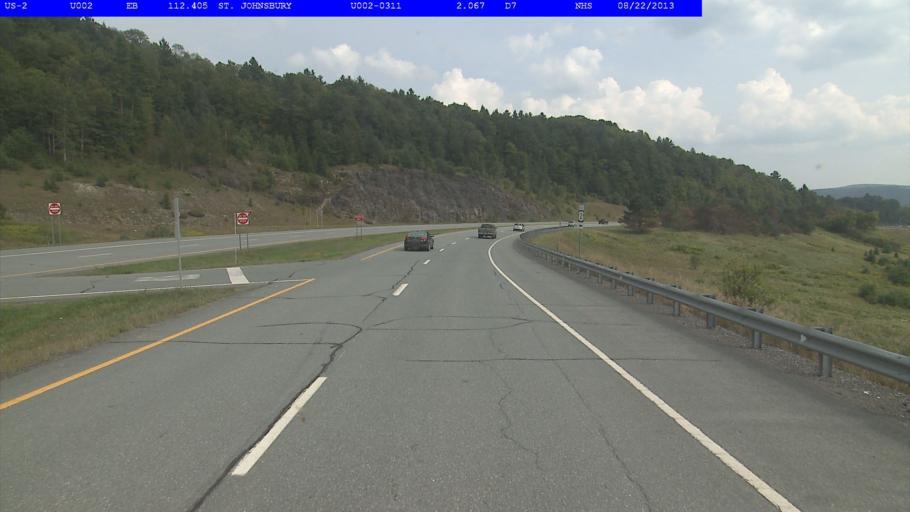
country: US
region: Vermont
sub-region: Caledonia County
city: St Johnsbury
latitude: 44.4276
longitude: -72.0329
